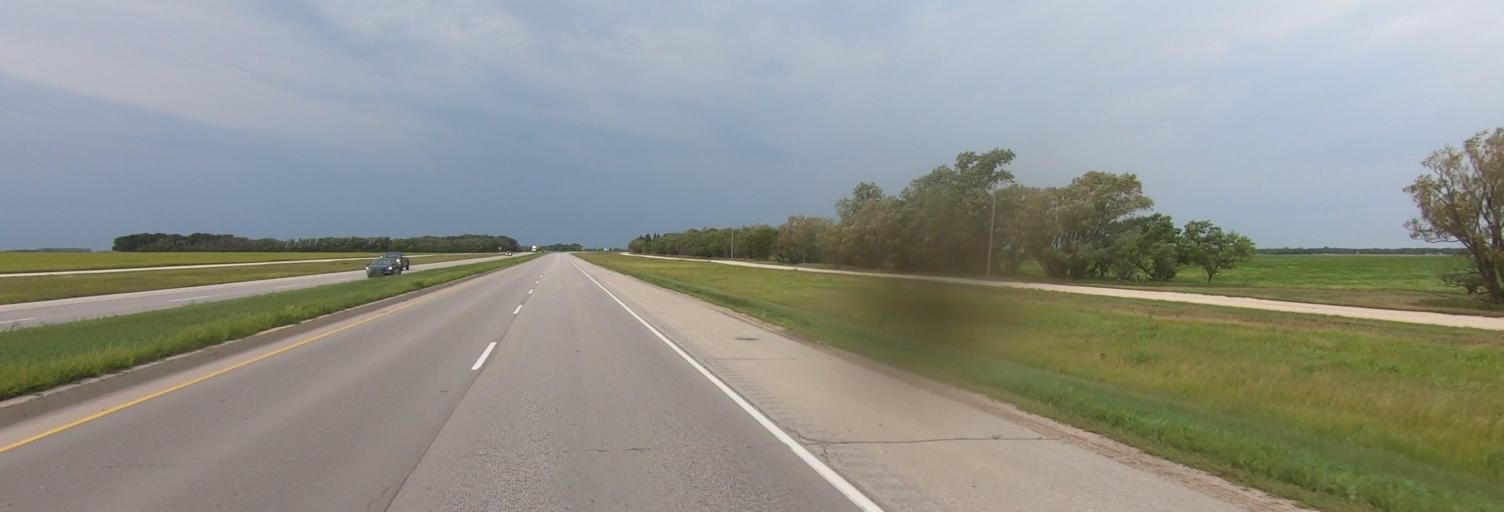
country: CA
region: Manitoba
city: Headingley
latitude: 49.7680
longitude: -97.2796
